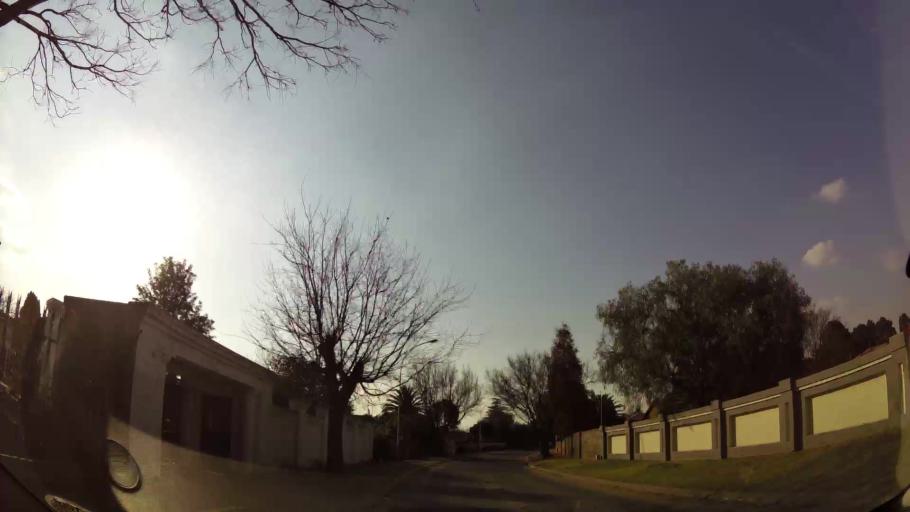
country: ZA
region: Gauteng
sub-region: Ekurhuleni Metropolitan Municipality
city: Benoni
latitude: -26.1333
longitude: 28.3675
